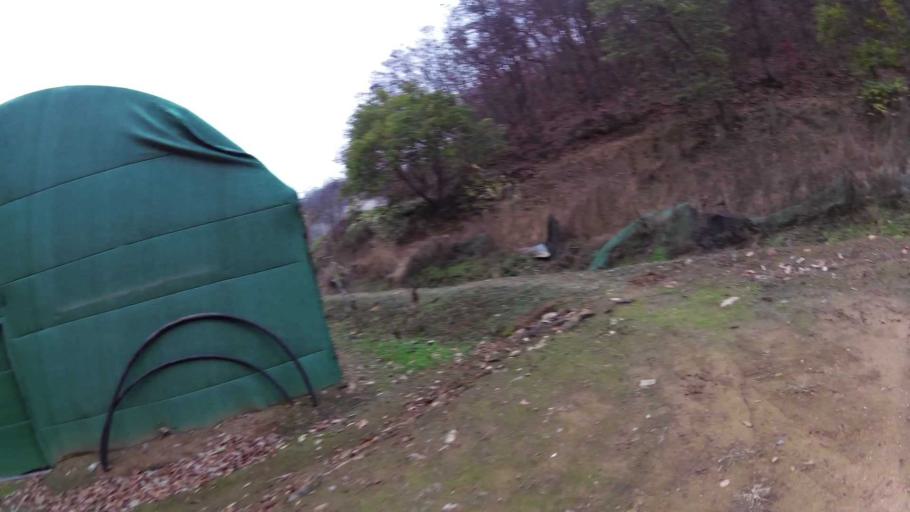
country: KR
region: Daegu
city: Daegu
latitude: 35.8593
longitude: 128.6594
